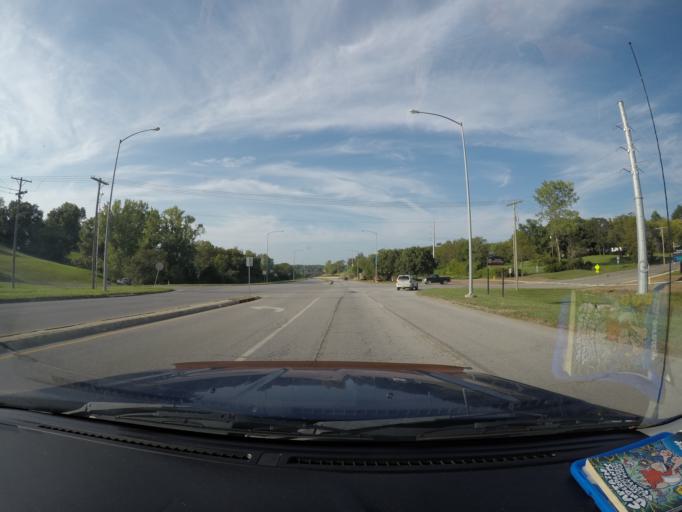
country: US
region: Kansas
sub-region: Atchison County
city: Atchison
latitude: 39.5466
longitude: -95.1296
